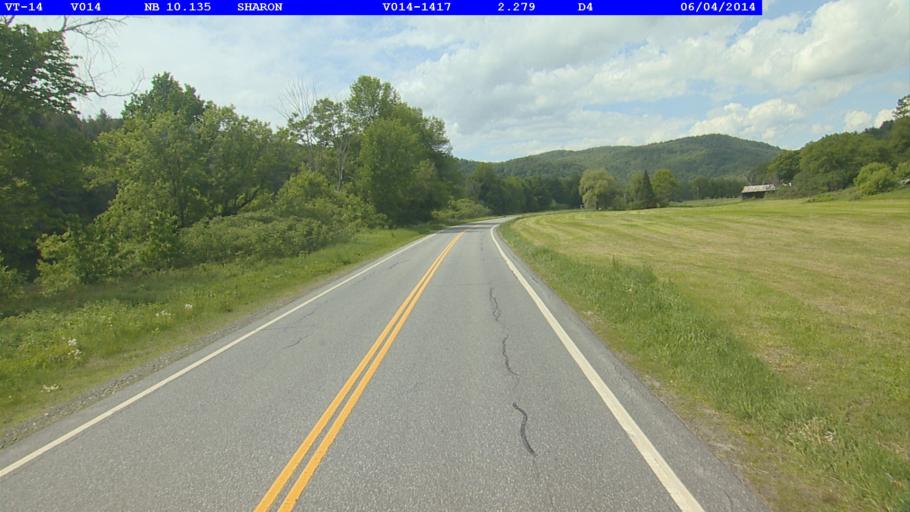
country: US
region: Vermont
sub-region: Windsor County
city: Woodstock
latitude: 43.7498
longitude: -72.4472
